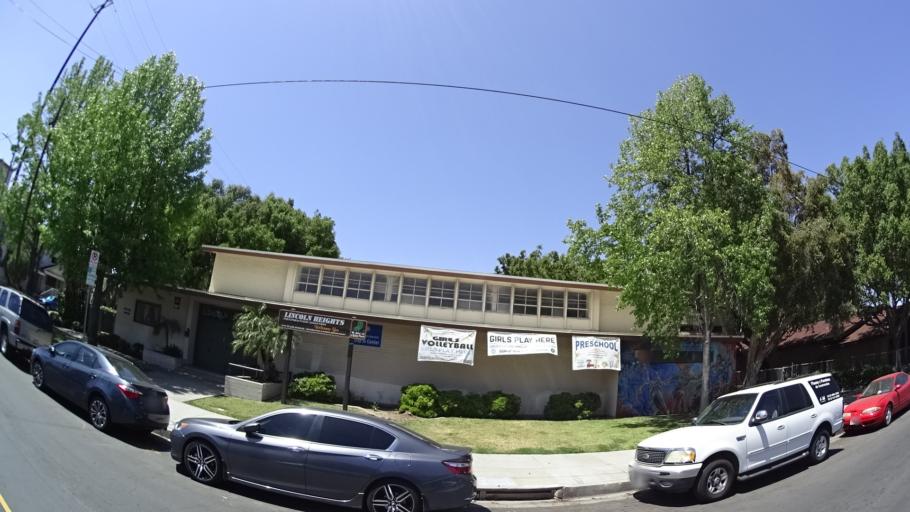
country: US
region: California
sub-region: Los Angeles County
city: Los Angeles
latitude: 34.0721
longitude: -118.2144
